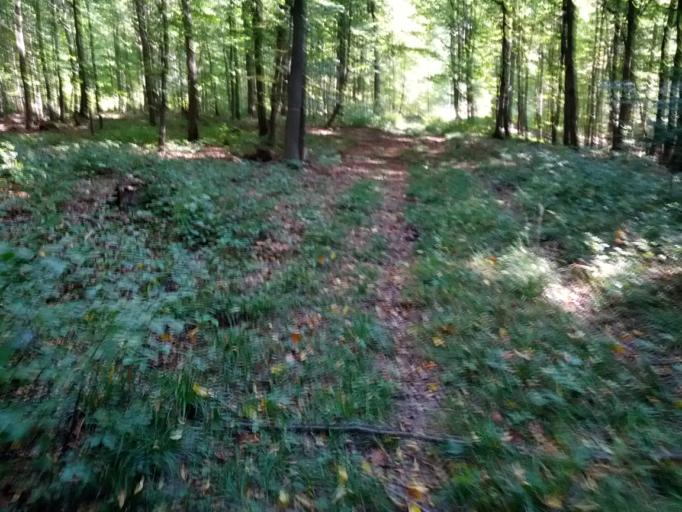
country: DE
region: Thuringia
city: Eisenach
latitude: 50.9986
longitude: 10.2927
